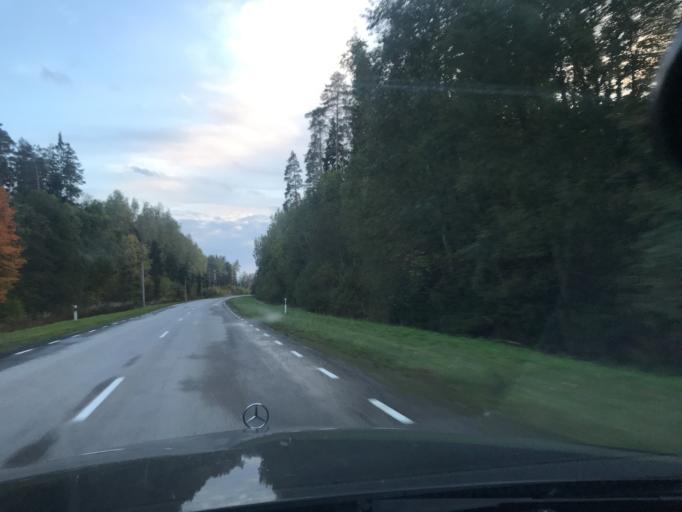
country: EE
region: Valgamaa
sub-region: Torva linn
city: Torva
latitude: 57.9975
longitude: 26.0781
